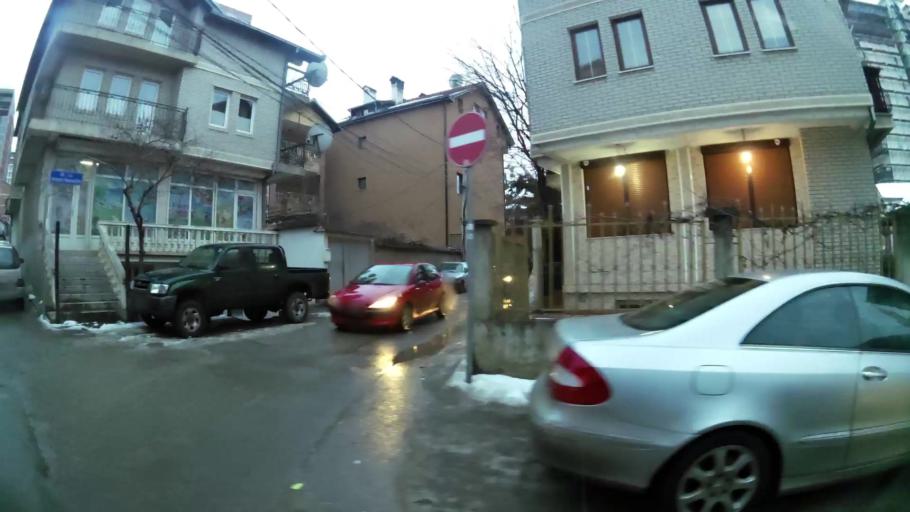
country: XK
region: Pristina
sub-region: Komuna e Prishtines
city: Pristina
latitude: 42.6588
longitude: 21.1683
